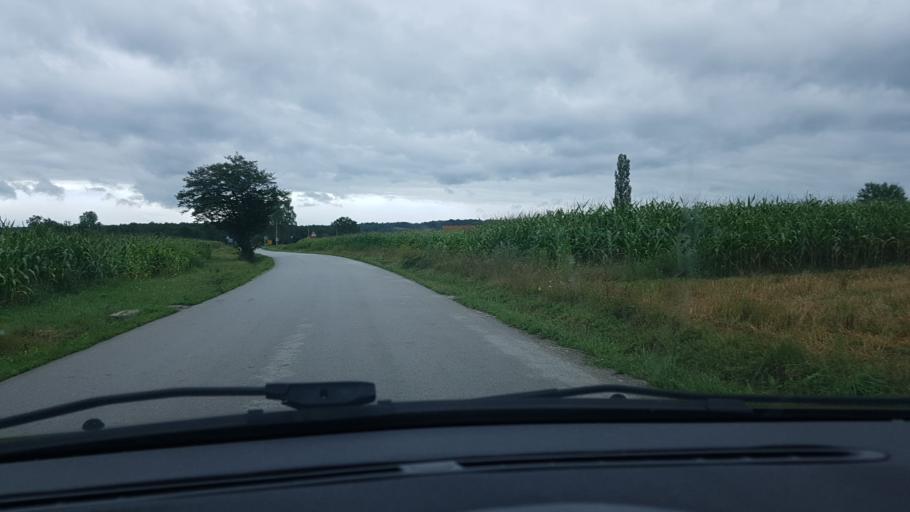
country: HR
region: Karlovacka
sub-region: Grad Karlovac
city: Karlovac
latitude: 45.5569
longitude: 15.5413
